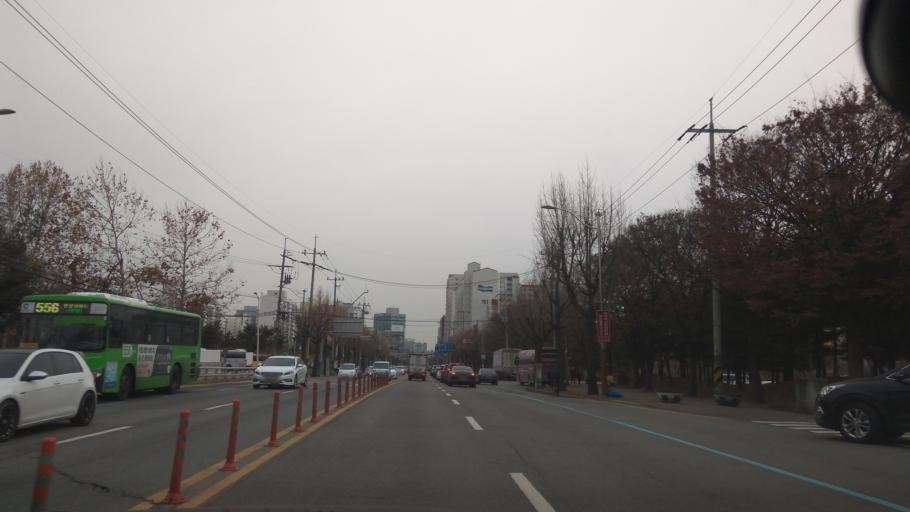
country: KR
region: Incheon
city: Incheon
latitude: 37.4910
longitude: 126.7133
